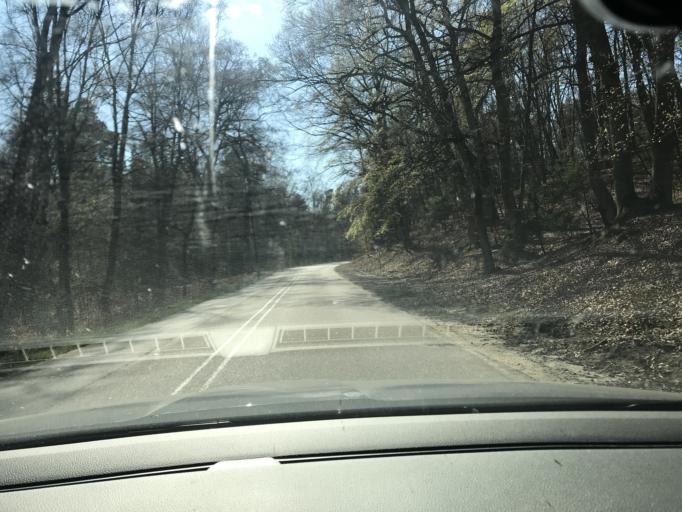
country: PL
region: Pomeranian Voivodeship
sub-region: Powiat nowodworski
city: Krynica Morska
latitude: 54.3648
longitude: 19.3693
